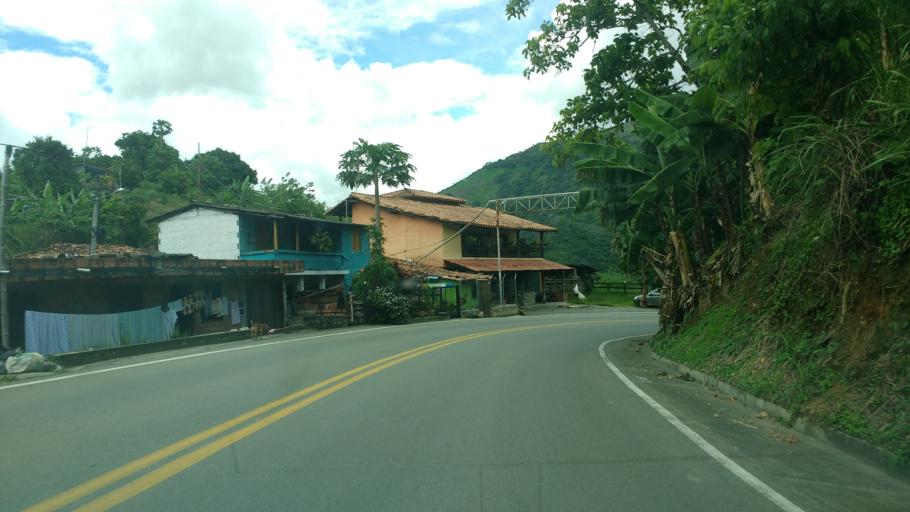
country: CO
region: Antioquia
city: Titiribi
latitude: 6.0635
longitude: -75.7503
